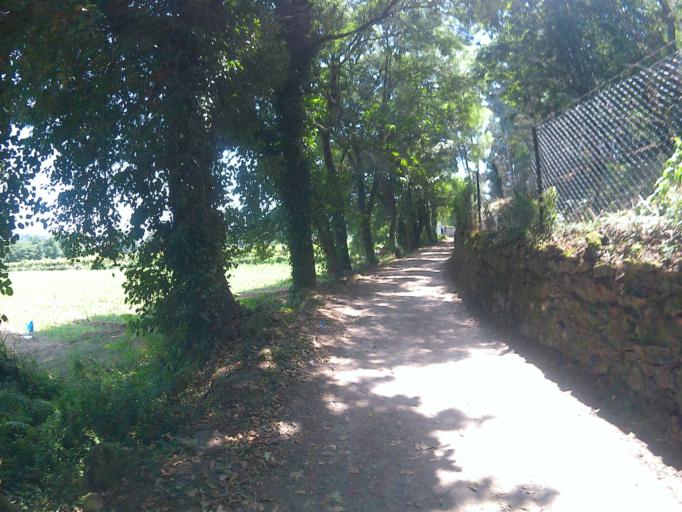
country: PT
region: Viana do Castelo
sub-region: Ponte de Lima
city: Ponte de Lima
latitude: 41.7748
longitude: -8.5689
